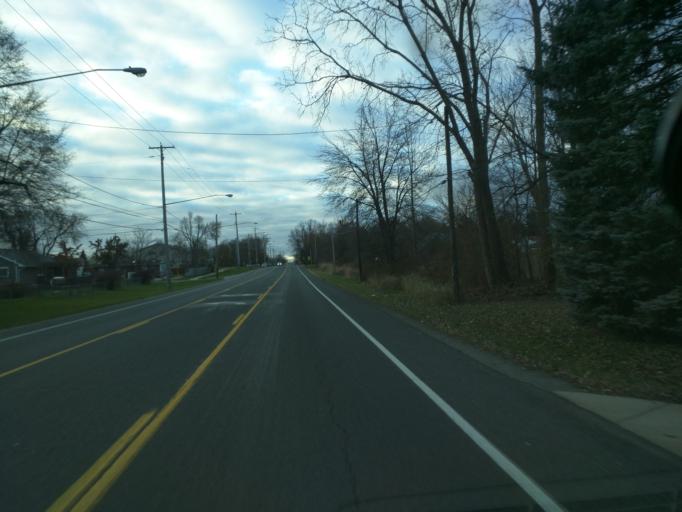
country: US
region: Michigan
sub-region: Eaton County
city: Dimondale
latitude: 42.6733
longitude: -84.6030
